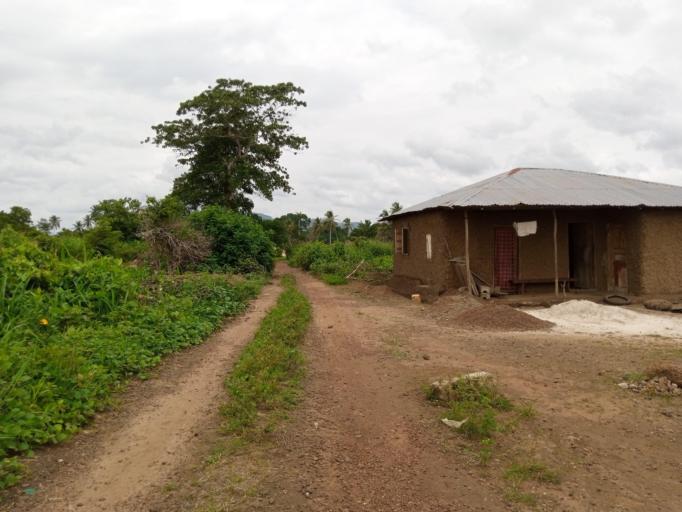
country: SL
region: Southern Province
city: Moyamba
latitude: 8.1613
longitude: -12.4245
